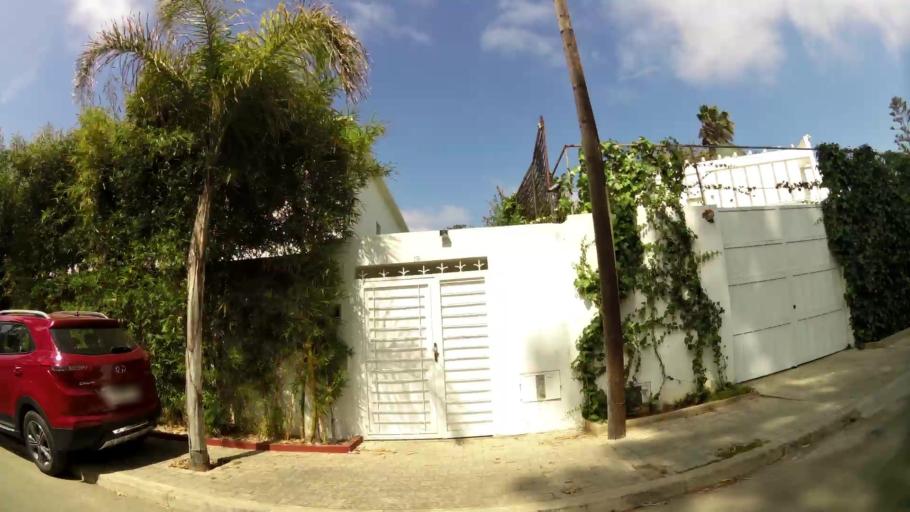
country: MA
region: Rabat-Sale-Zemmour-Zaer
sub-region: Rabat
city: Rabat
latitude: 33.9831
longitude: -6.8307
